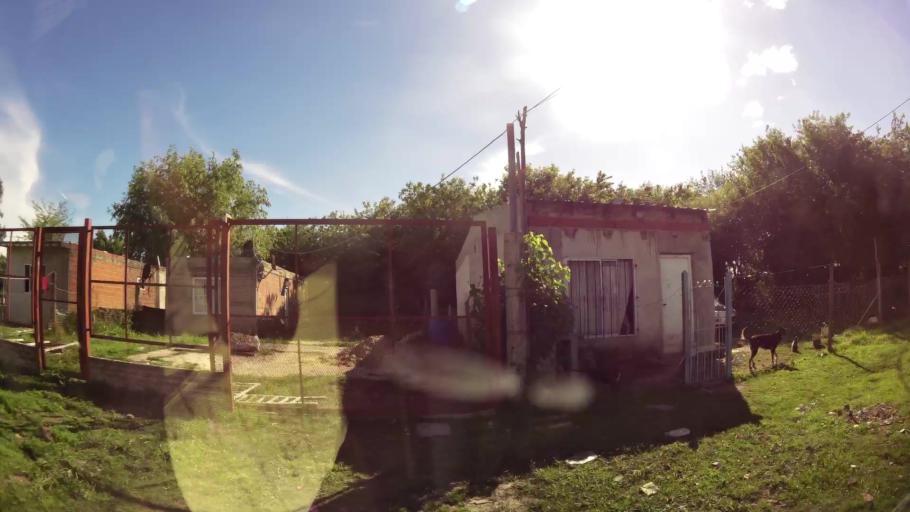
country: AR
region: Buenos Aires
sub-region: Partido de Almirante Brown
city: Adrogue
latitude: -34.8258
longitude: -58.3402
